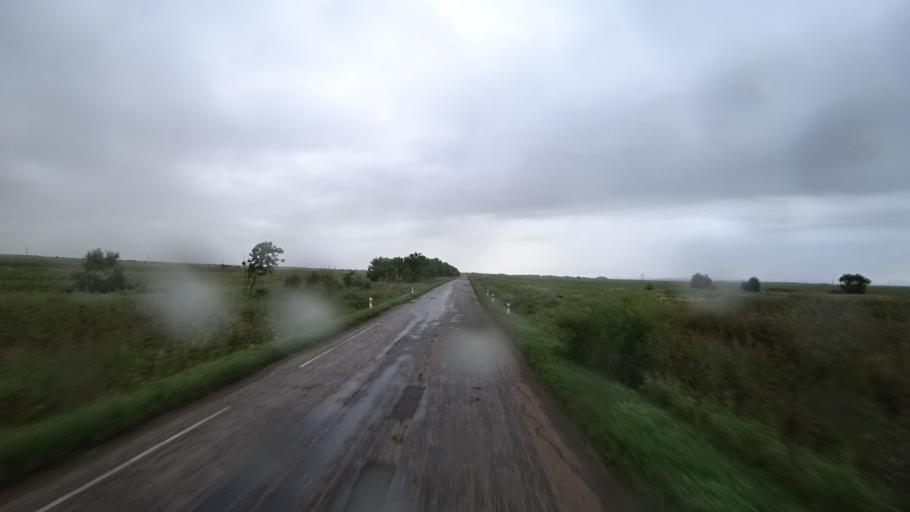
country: RU
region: Primorskiy
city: Chernigovka
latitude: 44.3811
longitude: 132.5296
